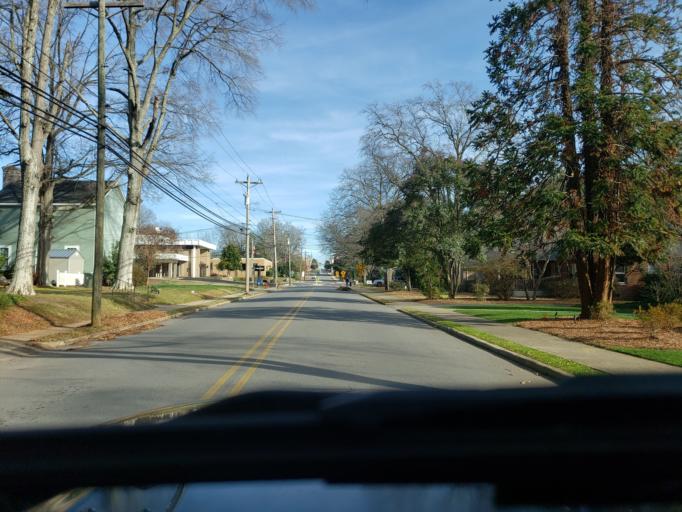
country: US
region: North Carolina
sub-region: Cleveland County
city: Kings Mountain
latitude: 35.2393
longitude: -81.3484
